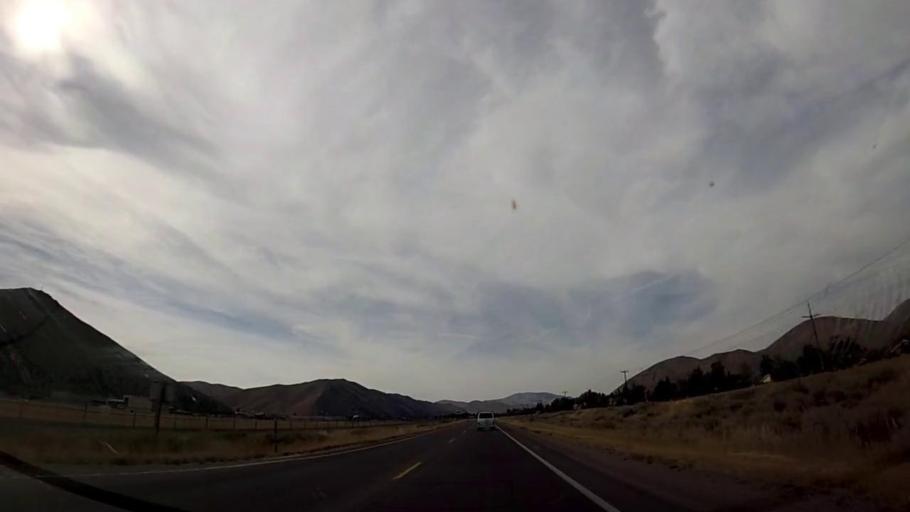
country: US
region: Idaho
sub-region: Blaine County
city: Hailey
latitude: 43.5044
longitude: -114.2944
